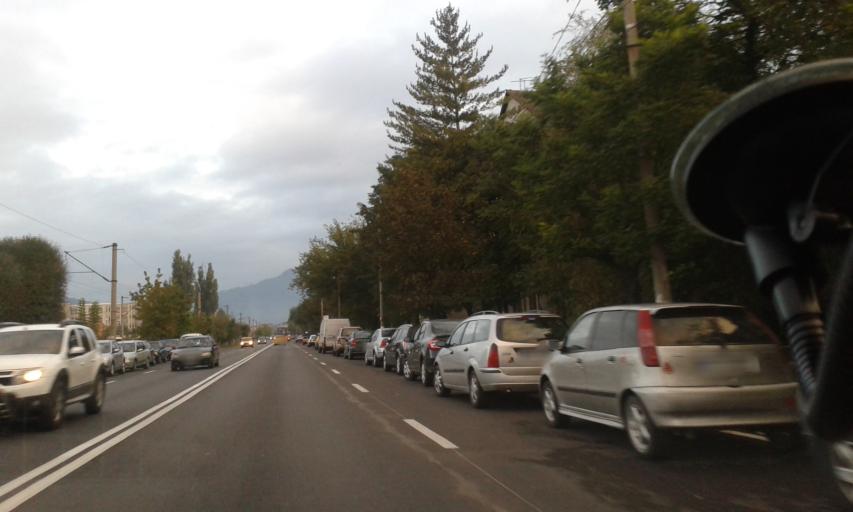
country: RO
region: Hunedoara
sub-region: Municipiul Petrosani
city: Petrosani
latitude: 45.3999
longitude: 23.3734
